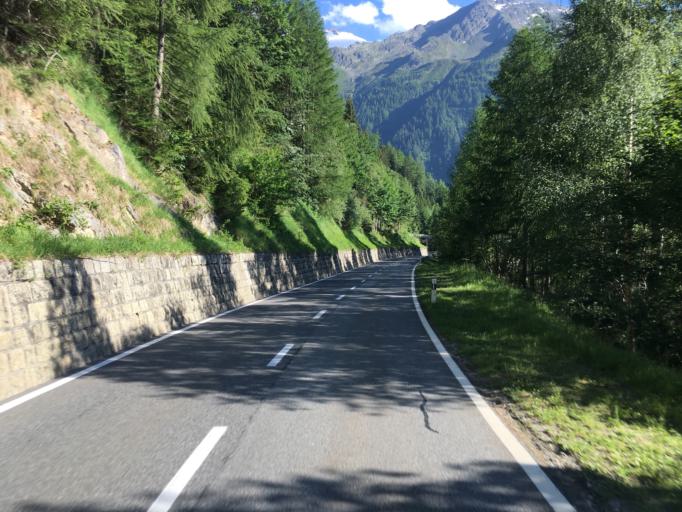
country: CH
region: Valais
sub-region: Martigny District
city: Martigny-Combe
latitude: 46.0549
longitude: 7.0000
